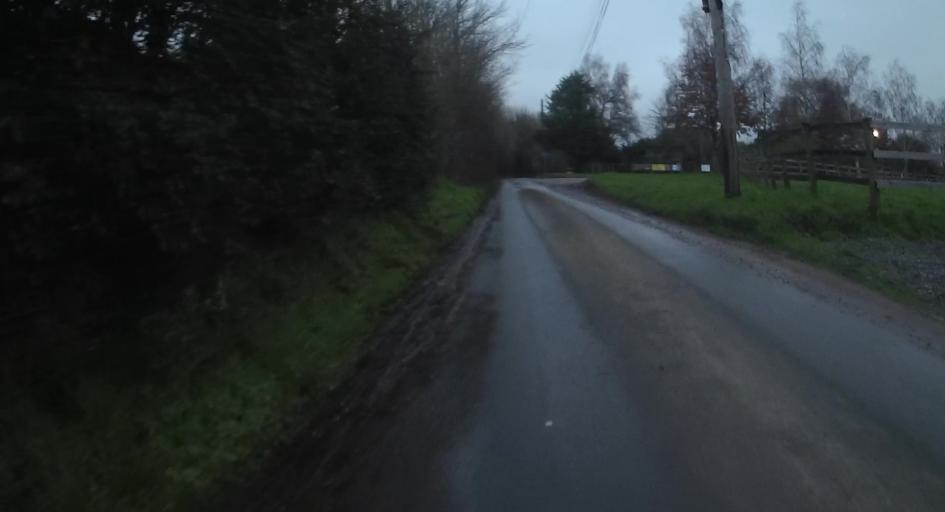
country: GB
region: England
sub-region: Hampshire
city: Tadley
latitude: 51.3381
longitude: -1.0896
